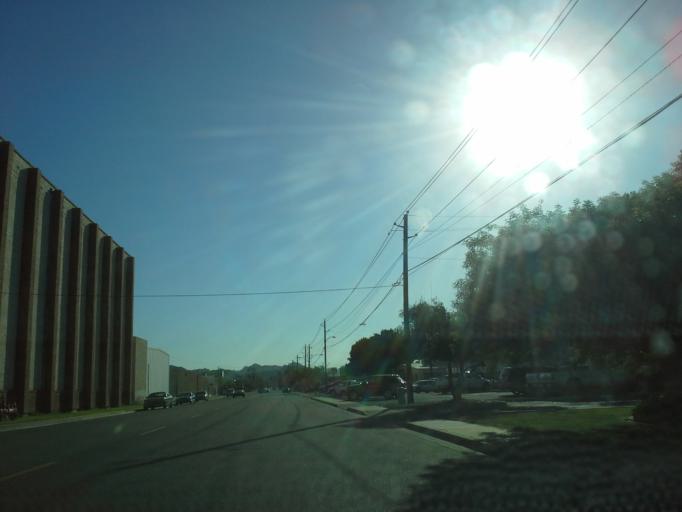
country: US
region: Arizona
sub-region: Maricopa County
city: Glendale
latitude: 33.5748
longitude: -112.1028
